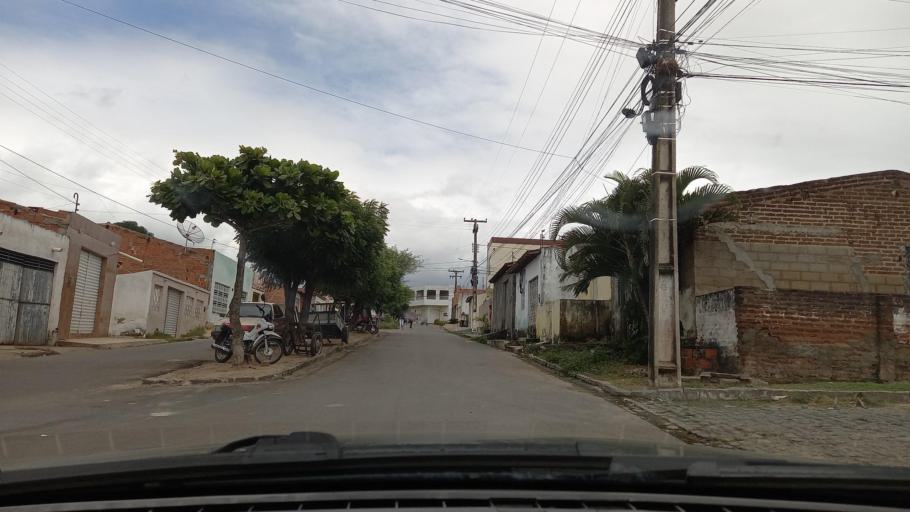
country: BR
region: Sergipe
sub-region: Caninde De Sao Francisco
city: Caninde de Sao Francisco
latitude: -9.6039
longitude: -37.7561
